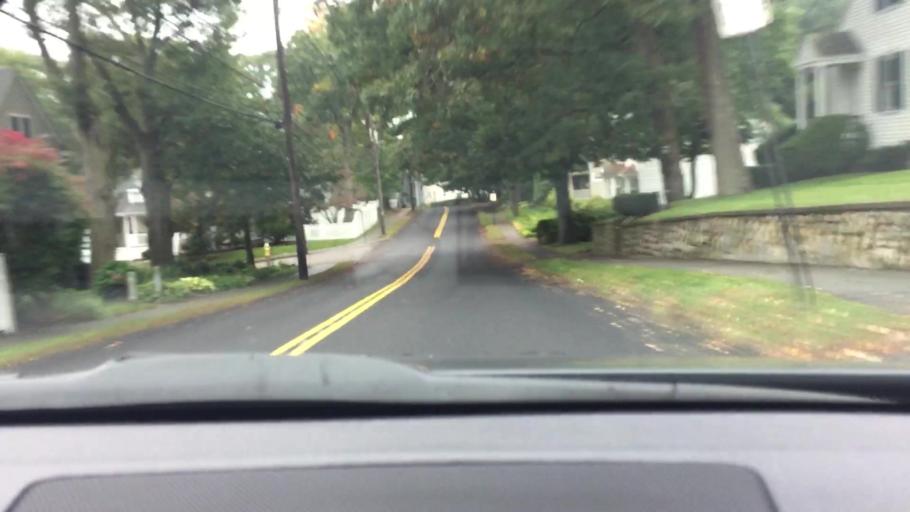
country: US
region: Massachusetts
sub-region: Norfolk County
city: Needham
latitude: 42.2876
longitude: -71.2242
